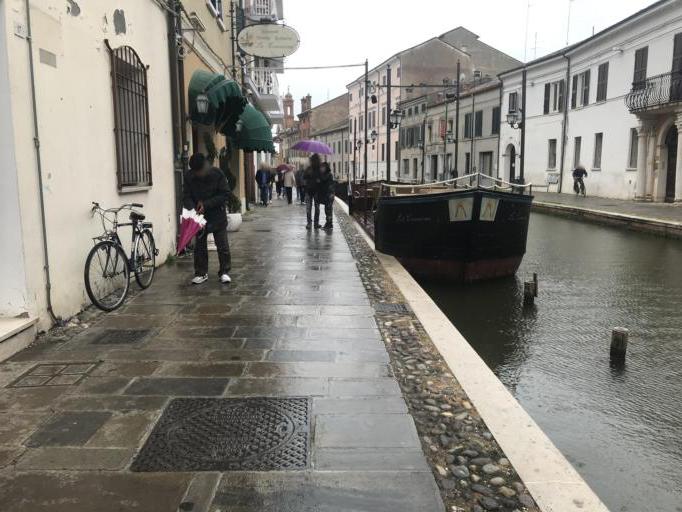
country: IT
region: Emilia-Romagna
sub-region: Provincia di Ferrara
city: Comacchio
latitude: 44.6945
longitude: 12.1827
